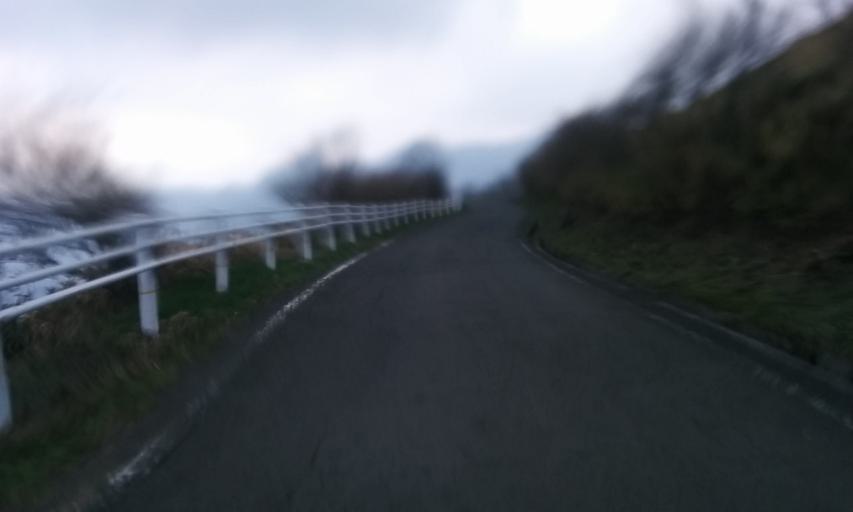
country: JP
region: Ehime
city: Saijo
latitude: 33.7788
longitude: 133.2201
